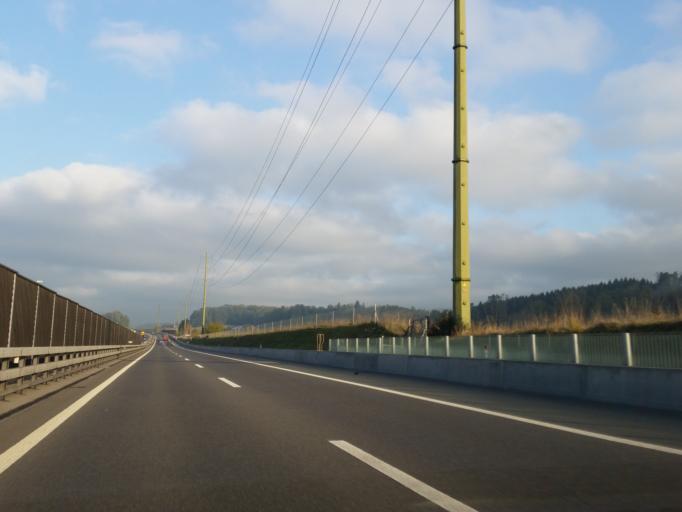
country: CH
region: Zurich
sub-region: Bezirk Affoltern
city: Knonau
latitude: 47.2205
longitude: 8.4672
